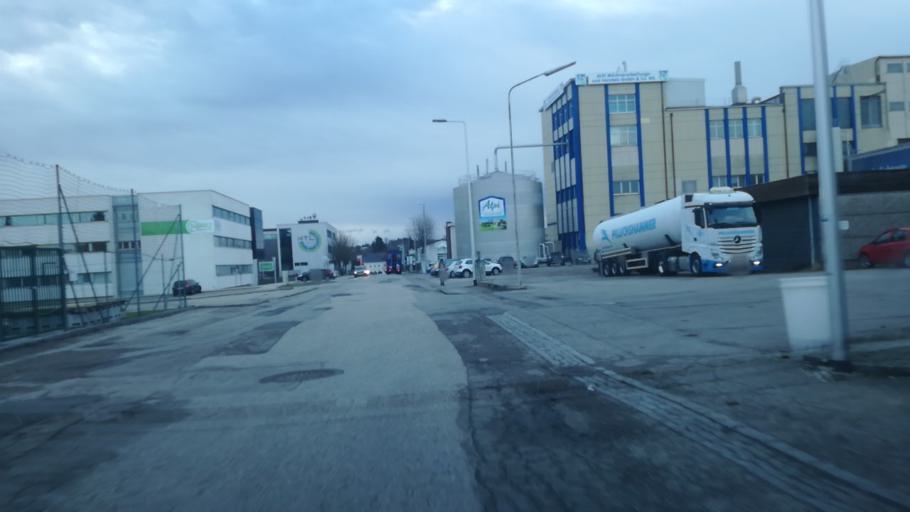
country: AT
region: Upper Austria
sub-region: Politischer Bezirk Ried im Innkreis
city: Ried im Innkreis
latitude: 48.2024
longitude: 13.4838
